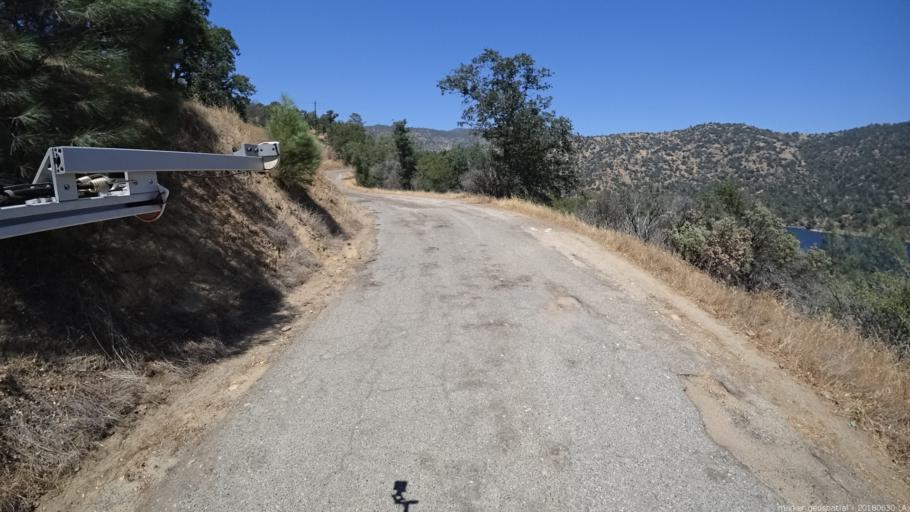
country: US
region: California
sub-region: Fresno County
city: Auberry
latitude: 37.1491
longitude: -119.4391
